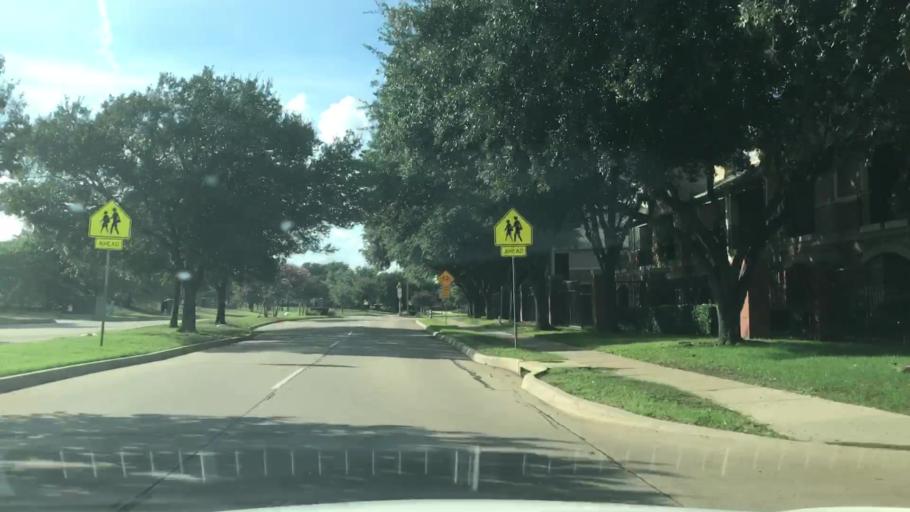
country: US
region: Texas
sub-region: Dallas County
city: Farmers Branch
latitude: 32.9240
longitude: -96.9561
